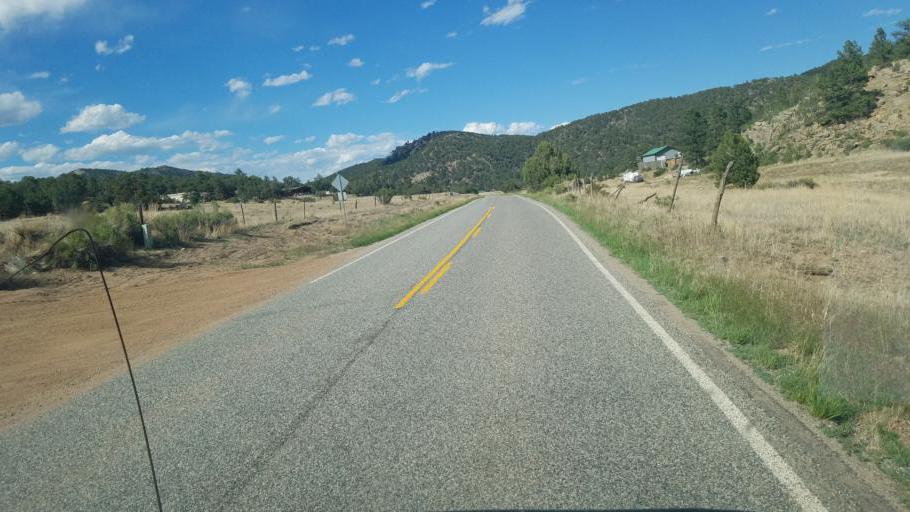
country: US
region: Colorado
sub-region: Fremont County
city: Canon City
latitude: 38.3683
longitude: -105.4606
